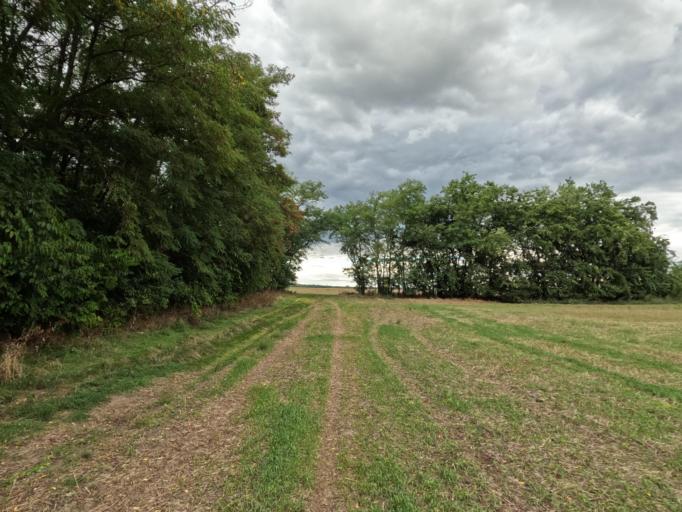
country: HU
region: Tolna
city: Tengelic
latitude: 46.5228
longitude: 18.6749
